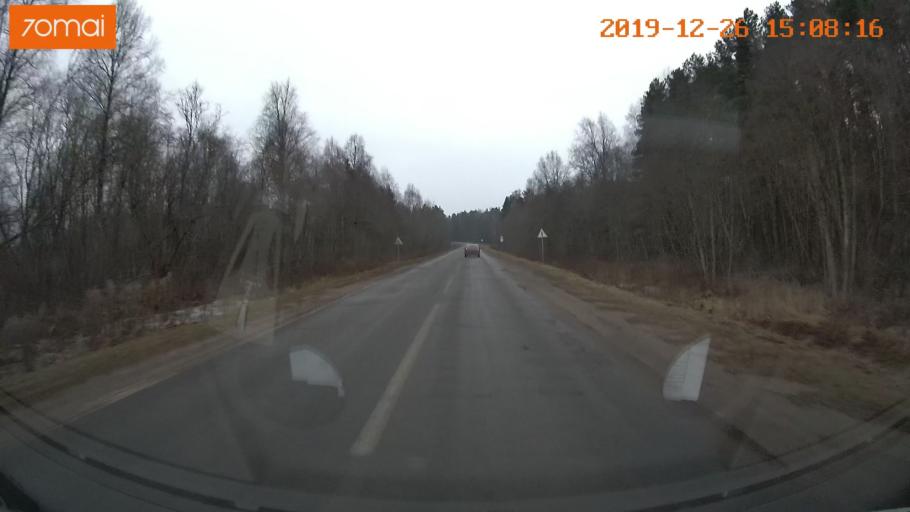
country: RU
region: Jaroslavl
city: Rybinsk
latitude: 58.1615
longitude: 38.8392
